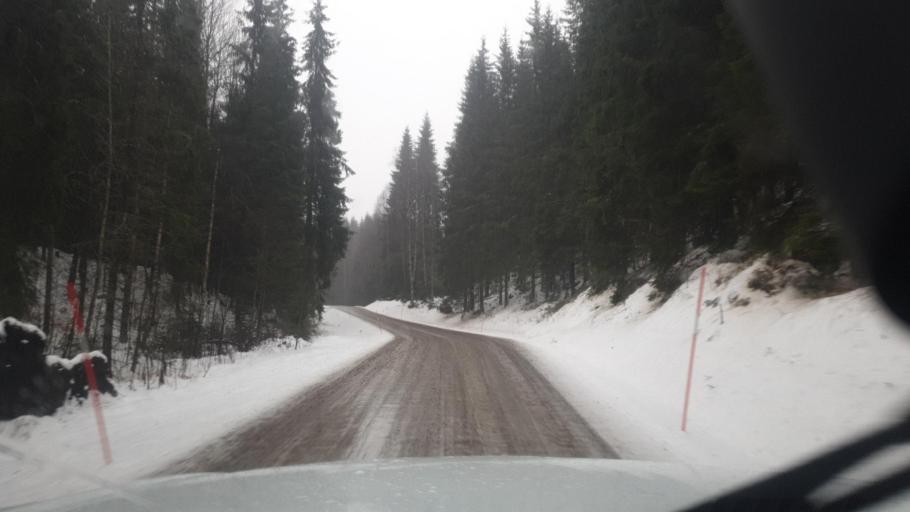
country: SE
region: Vaermland
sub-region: Eda Kommun
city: Charlottenberg
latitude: 60.0647
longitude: 12.5417
